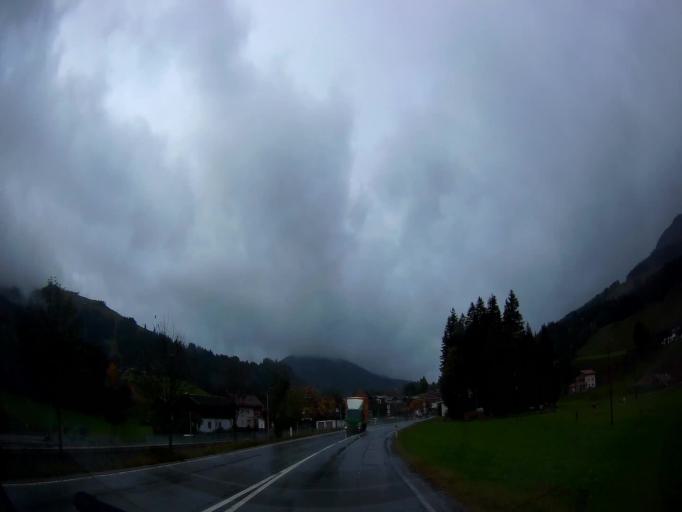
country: AT
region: Salzburg
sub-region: Politischer Bezirk Zell am See
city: Leogang
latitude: 47.4404
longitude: 12.7328
